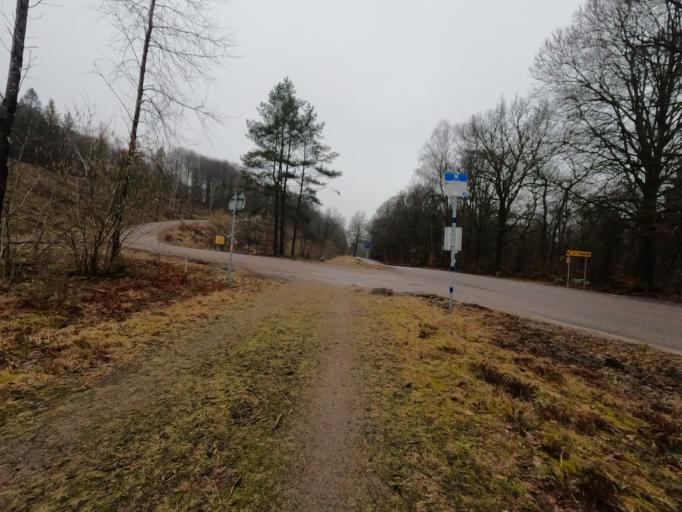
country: SE
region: Halland
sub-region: Halmstads Kommun
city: Oskarstrom
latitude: 56.7565
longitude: 13.1714
